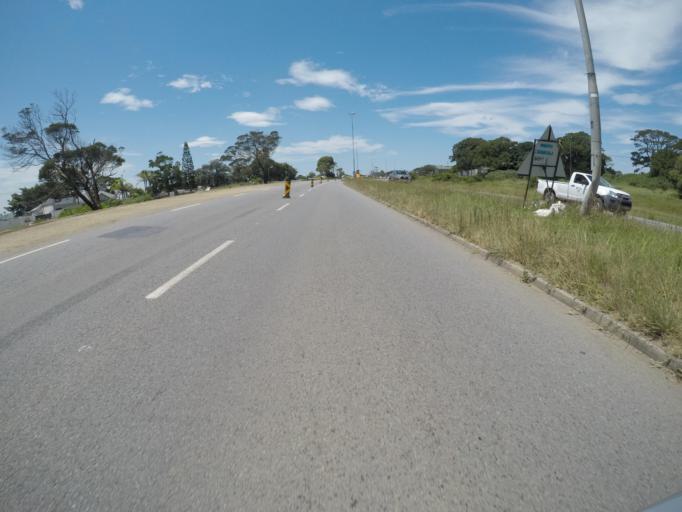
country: ZA
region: Eastern Cape
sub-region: Buffalo City Metropolitan Municipality
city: East London
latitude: -33.0351
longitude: 27.8416
